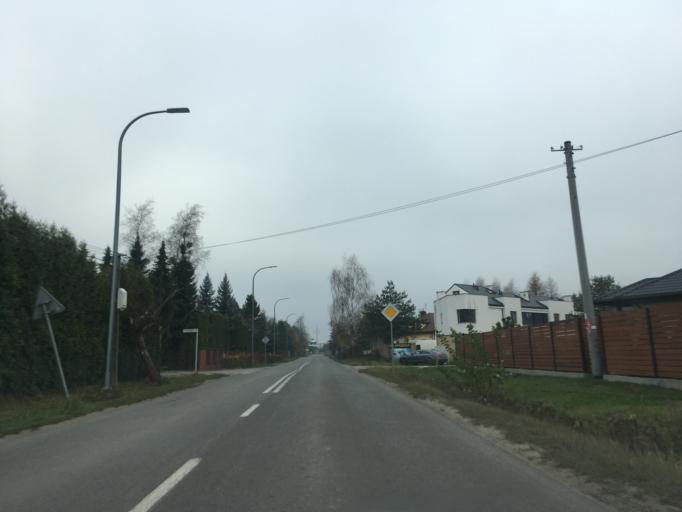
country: PL
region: Masovian Voivodeship
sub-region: Powiat piaseczynski
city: Lesznowola
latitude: 52.0703
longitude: 20.9646
